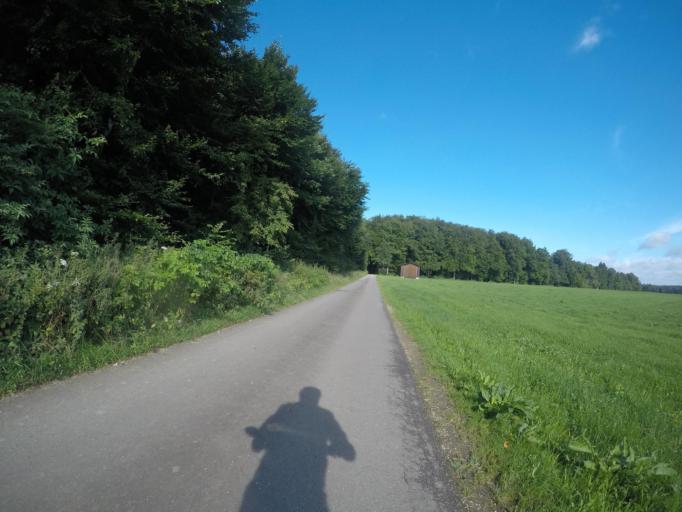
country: DE
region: Baden-Wuerttemberg
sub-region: Tuebingen Region
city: Schelklingen
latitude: 48.3939
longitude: 9.6946
